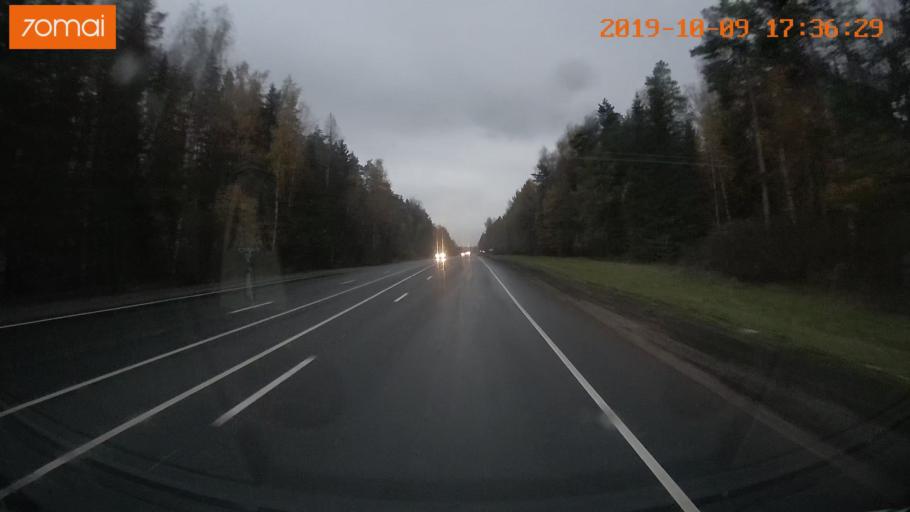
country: RU
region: Ivanovo
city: Bogorodskoye
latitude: 57.0777
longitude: 40.9967
